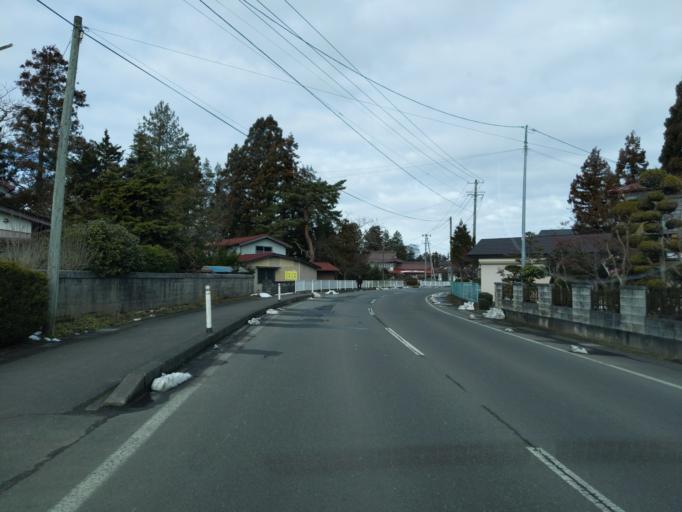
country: JP
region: Iwate
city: Mizusawa
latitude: 39.0724
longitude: 141.1636
